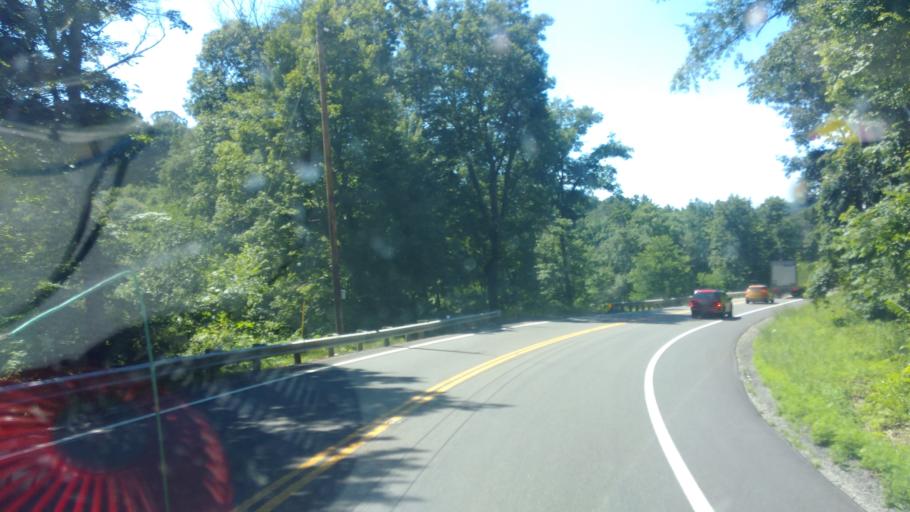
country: US
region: Ohio
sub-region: Carroll County
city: Carrollton
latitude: 40.4979
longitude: -80.9761
